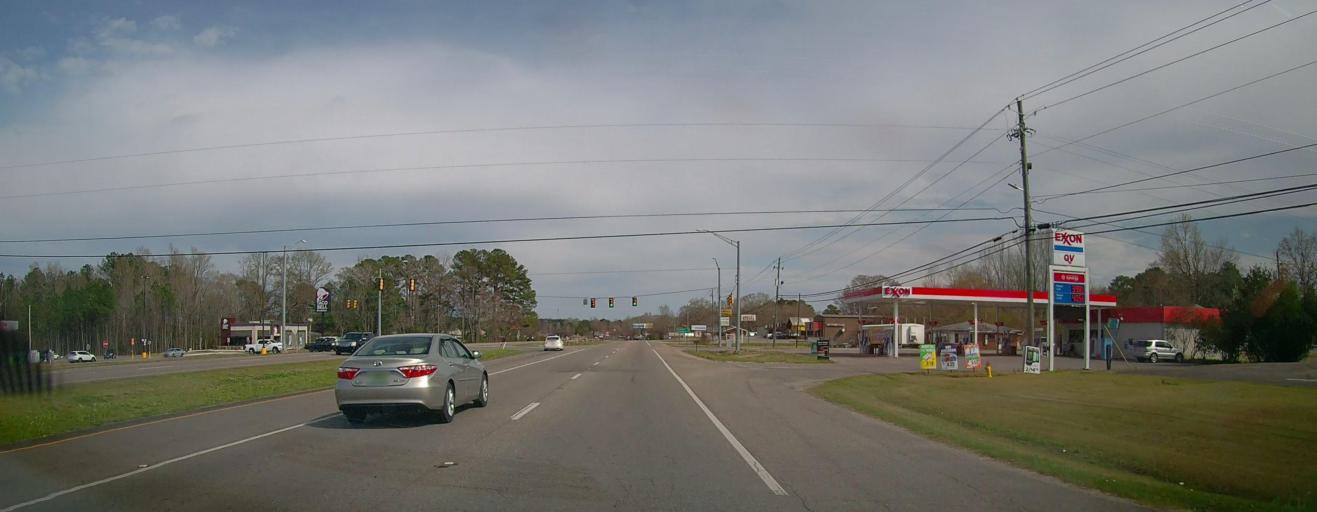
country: US
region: Alabama
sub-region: Walker County
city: Sumiton
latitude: 33.7434
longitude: -87.0431
